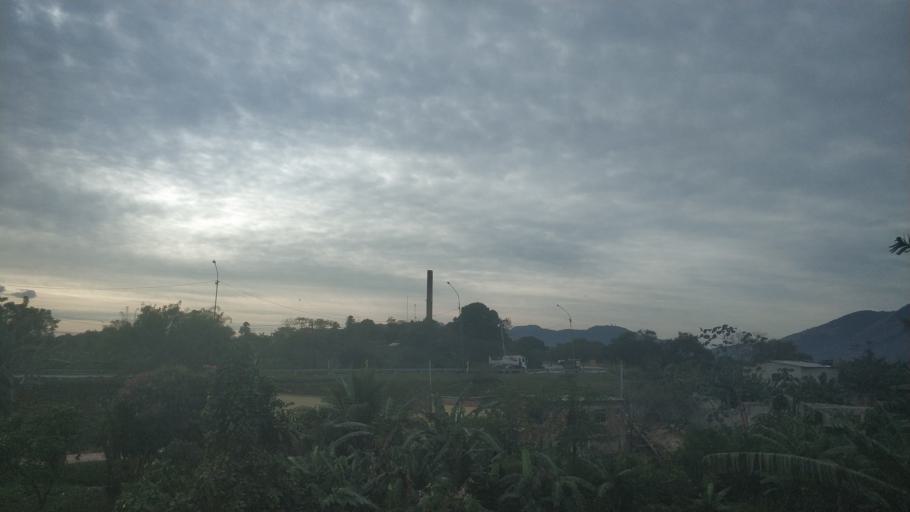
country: BR
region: Rio de Janeiro
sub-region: Seropedica
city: Seropedica
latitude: -22.8118
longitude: -43.6315
